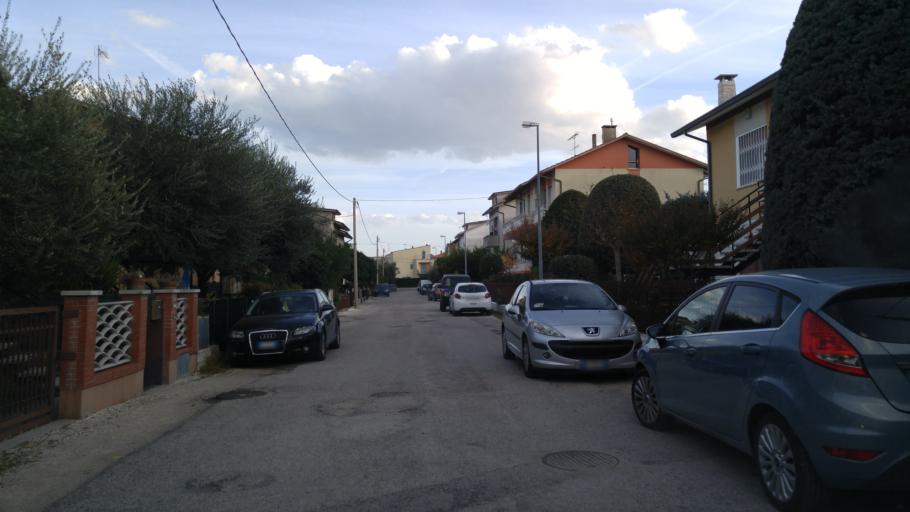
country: IT
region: The Marches
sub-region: Provincia di Pesaro e Urbino
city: Fano
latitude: 43.8315
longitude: 13.0101
